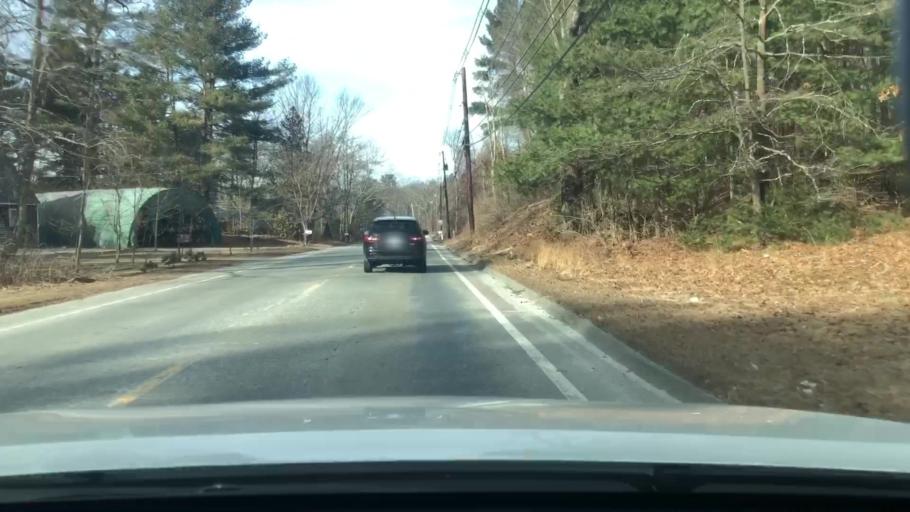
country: US
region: Massachusetts
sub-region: Worcester County
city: Northbridge
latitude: 42.1870
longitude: -71.6499
